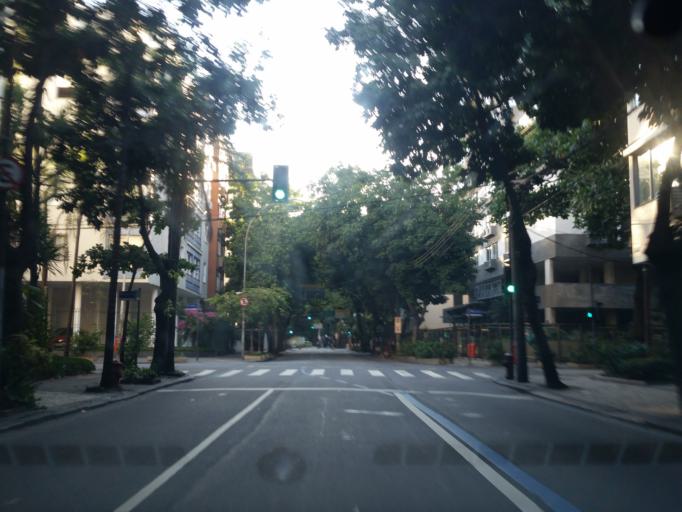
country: BR
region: Rio de Janeiro
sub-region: Rio De Janeiro
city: Rio de Janeiro
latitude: -22.9848
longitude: -43.2183
